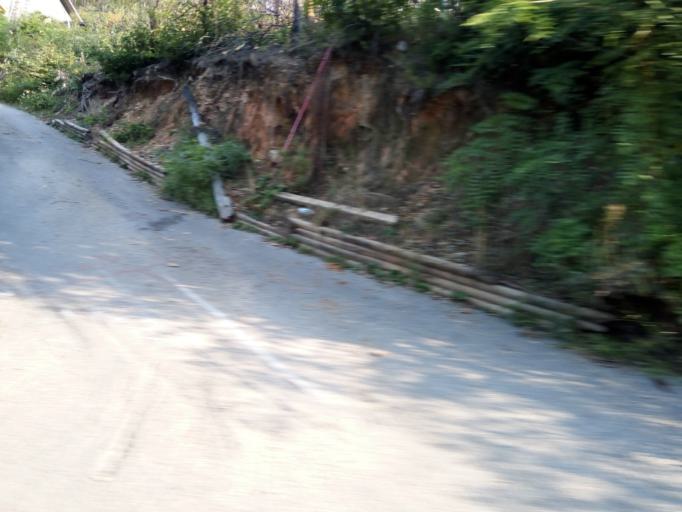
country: US
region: Tennessee
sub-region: Sevier County
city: Gatlinburg
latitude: 35.7200
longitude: -83.5309
